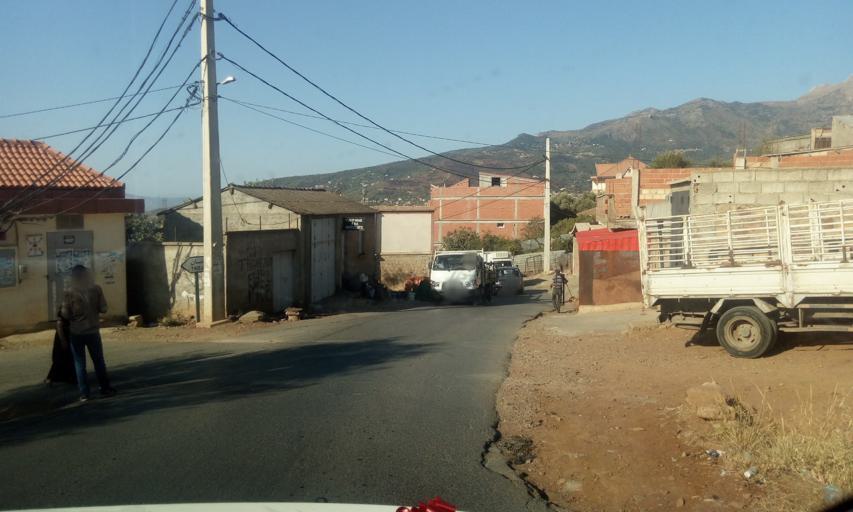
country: DZ
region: Tizi Ouzou
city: Chemini
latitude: 36.5677
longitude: 4.6165
